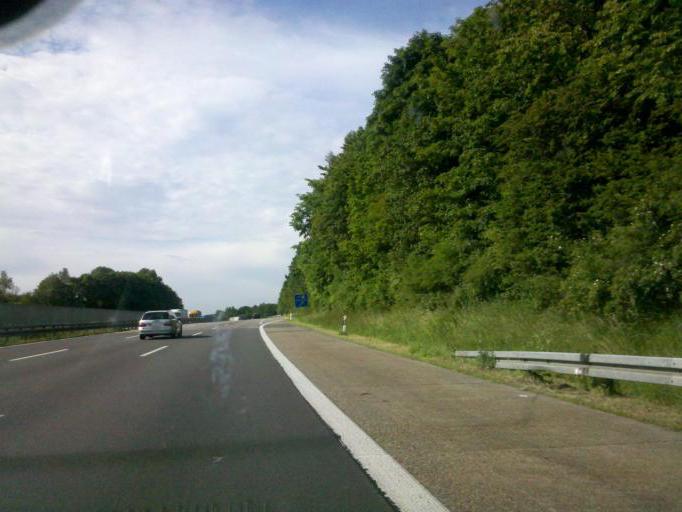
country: DE
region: North Rhine-Westphalia
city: Meinerzhagen
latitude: 51.0737
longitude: 7.6977
